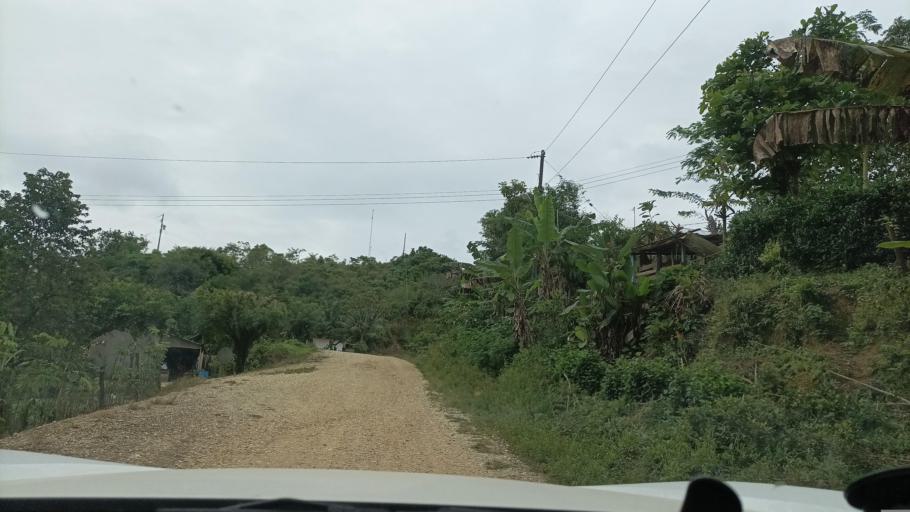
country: MX
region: Veracruz
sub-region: Uxpanapa
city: Poblado 10
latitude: 17.5653
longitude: -94.4250
